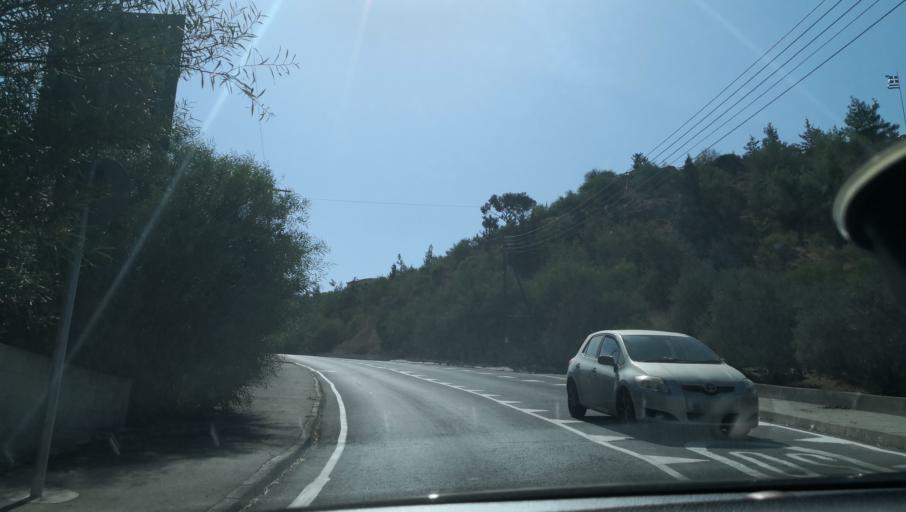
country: CY
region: Lefkosia
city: Mammari
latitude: 35.1720
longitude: 33.2021
